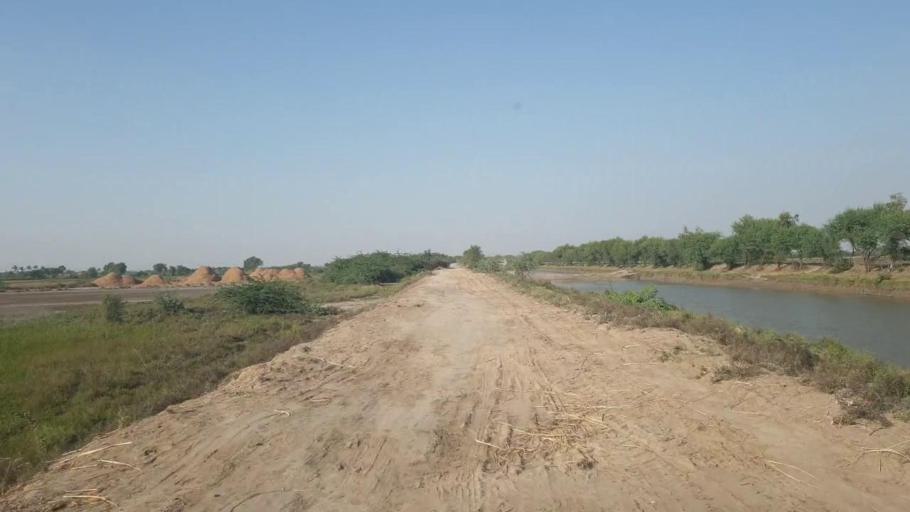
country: PK
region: Sindh
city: Badin
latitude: 24.6356
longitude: 68.8150
